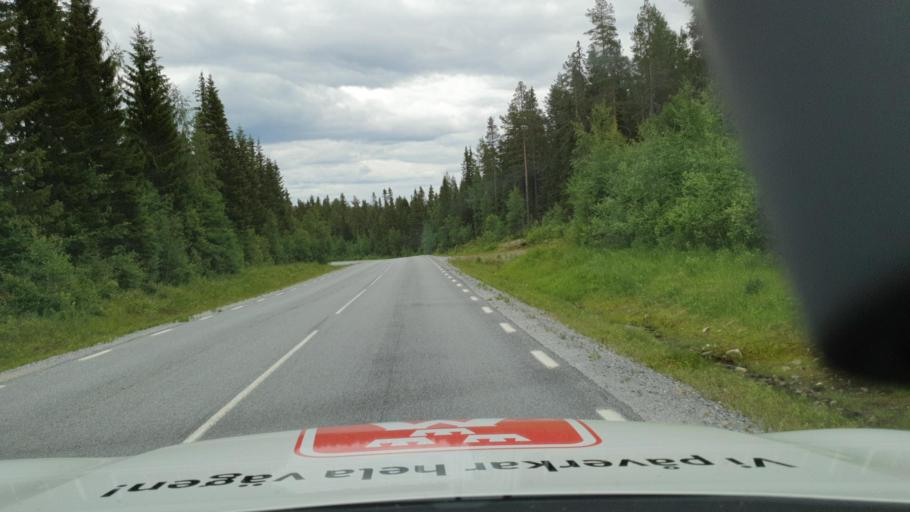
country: SE
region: Vaesterbotten
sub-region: Bjurholms Kommun
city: Bjurholm
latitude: 63.8832
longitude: 19.0493
